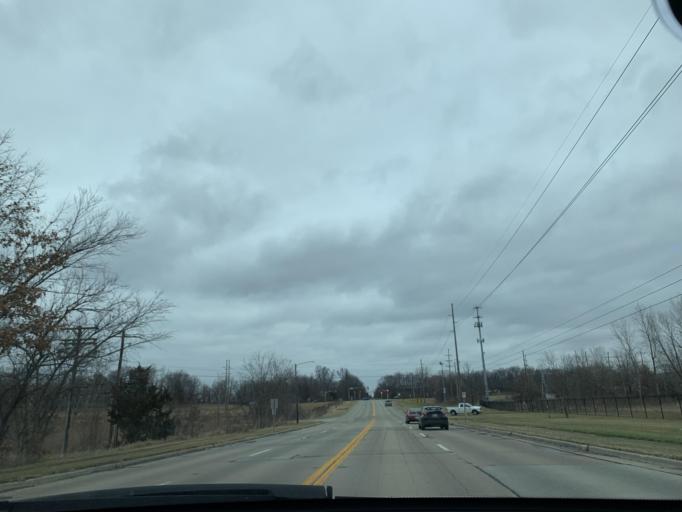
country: US
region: Illinois
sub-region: Sangamon County
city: Leland Grove
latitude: 39.8223
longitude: -89.6872
